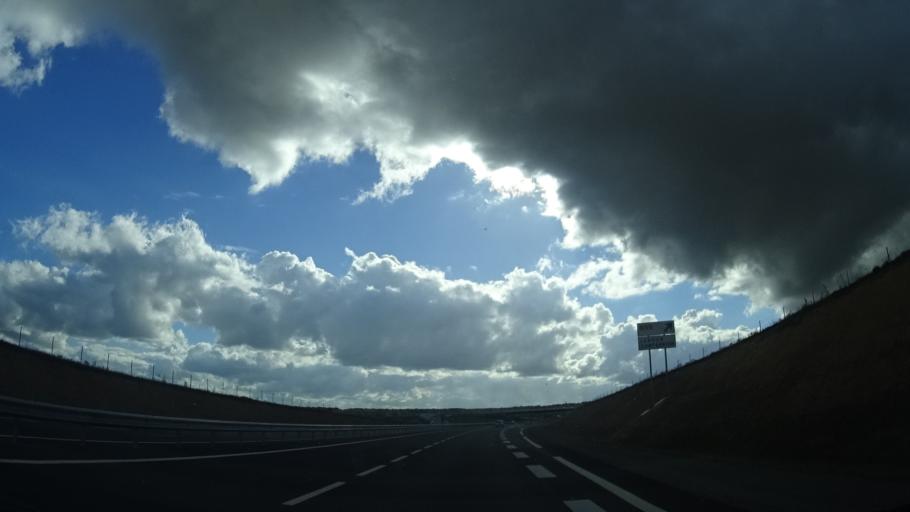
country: FR
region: Brittany
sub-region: Departement d'Ille-et-Vilaine
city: Pipriac
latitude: 47.7832
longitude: -1.9245
